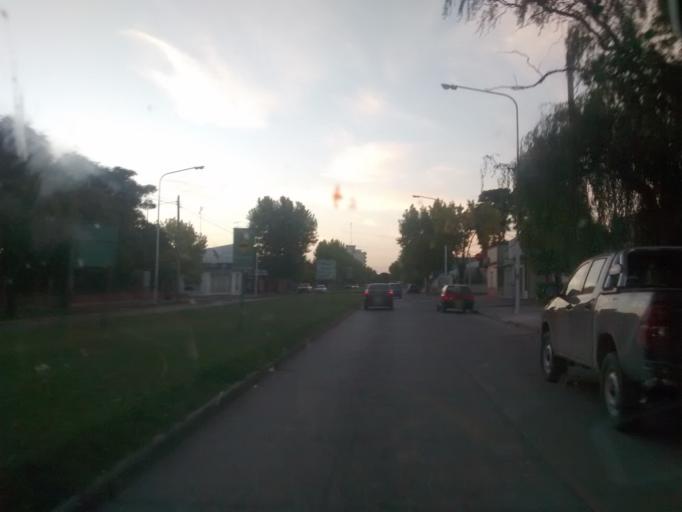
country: AR
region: Buenos Aires
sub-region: Partido de Loberia
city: Loberia
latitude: -38.1683
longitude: -58.7767
